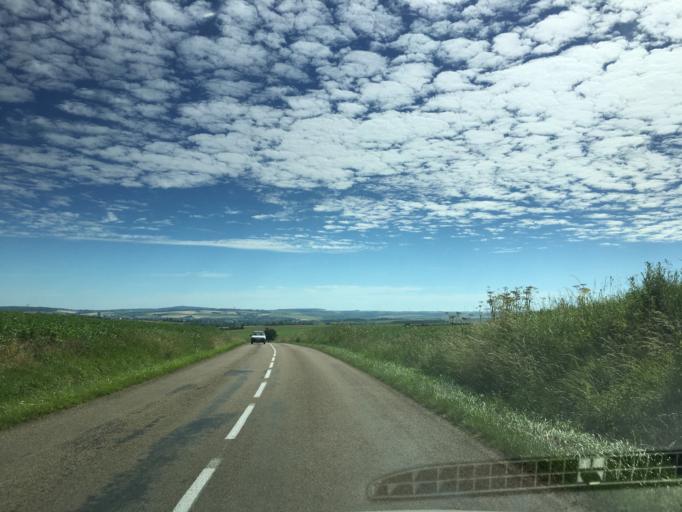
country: FR
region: Bourgogne
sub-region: Departement de l'Yonne
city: Saint-Georges-sur-Baulche
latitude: 47.7680
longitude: 3.5277
